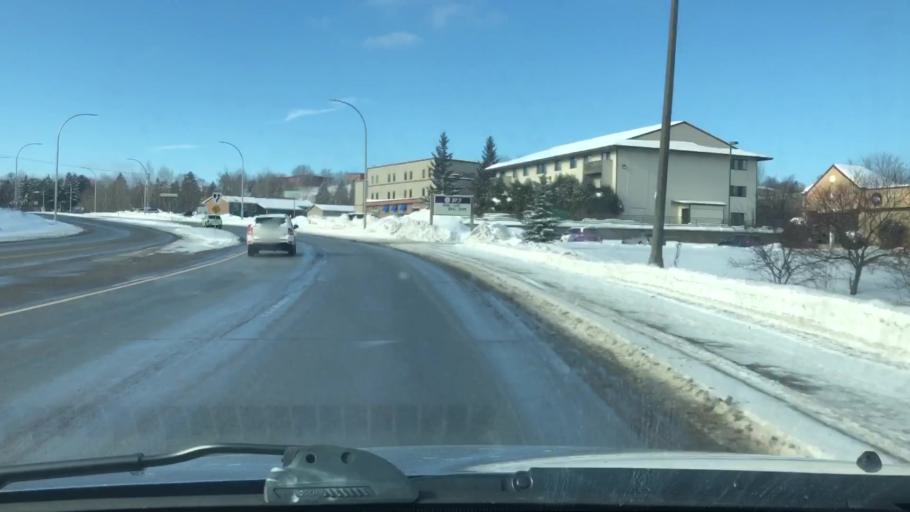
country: US
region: Minnesota
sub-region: Saint Louis County
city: Duluth
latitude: 46.7990
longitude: -92.1110
